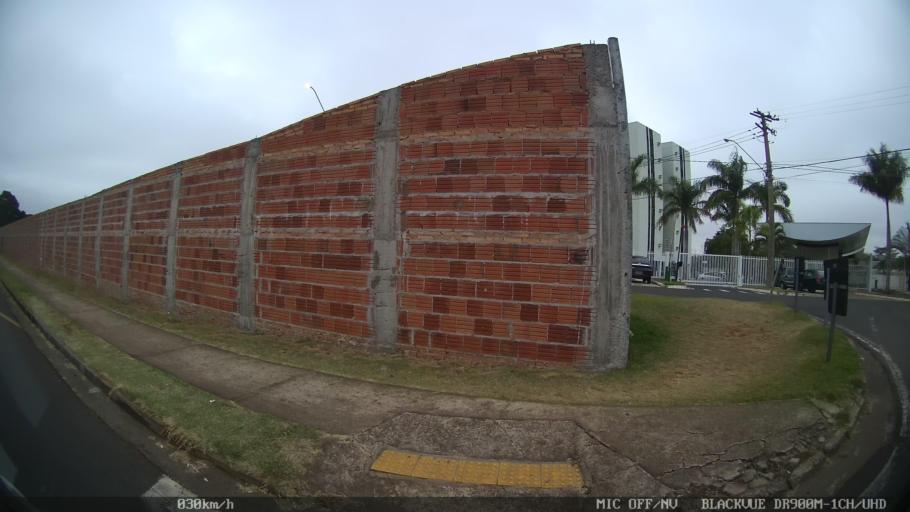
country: BR
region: Sao Paulo
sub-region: Sao Jose Do Rio Preto
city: Sao Jose do Rio Preto
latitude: -20.8528
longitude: -49.4047
